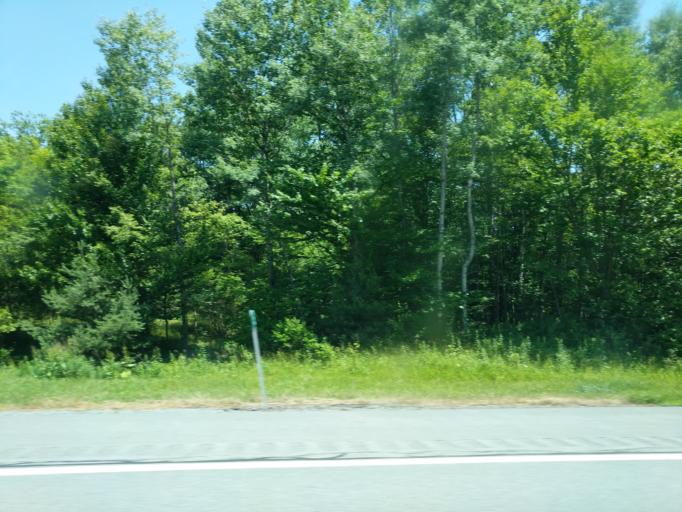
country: US
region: New York
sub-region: Sullivan County
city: Livingston Manor
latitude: 41.9189
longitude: -74.8399
